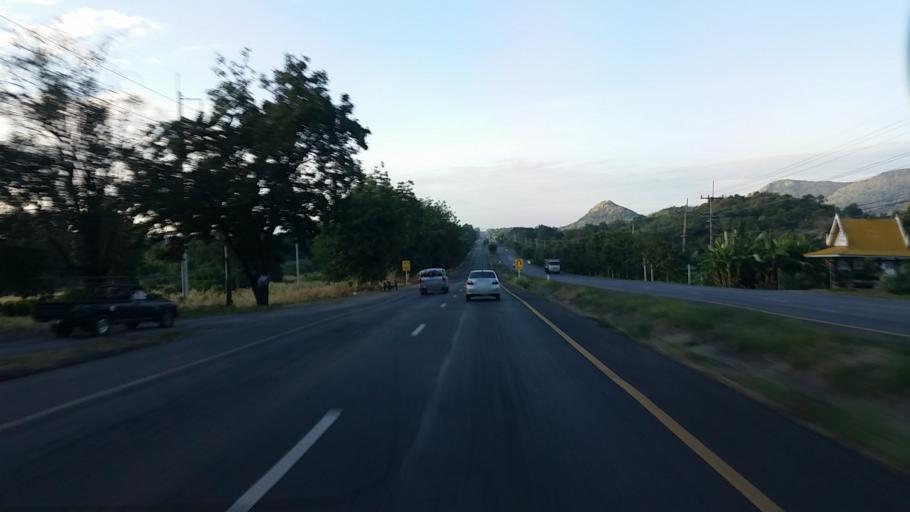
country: TH
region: Lop Buri
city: Chai Badan
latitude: 15.1540
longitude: 101.0550
